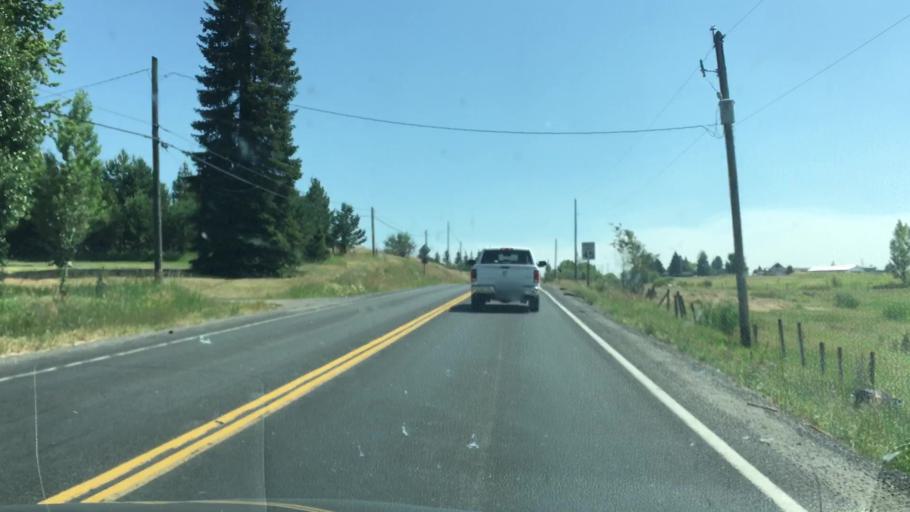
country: US
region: Idaho
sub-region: Valley County
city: McCall
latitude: 44.8884
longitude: -116.0925
